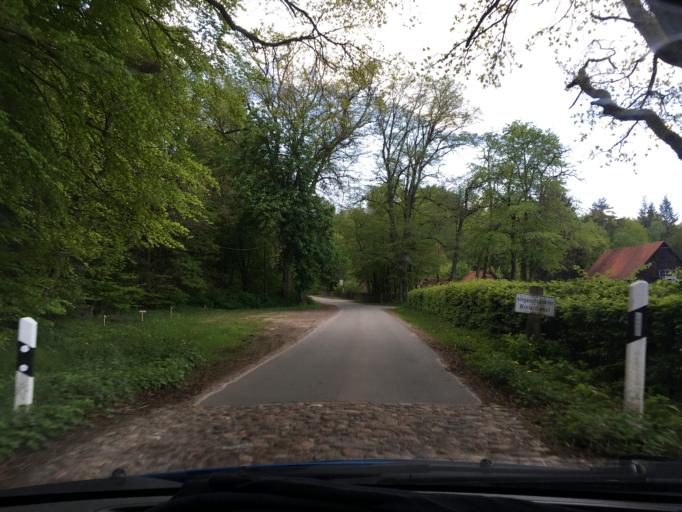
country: DE
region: Lower Saxony
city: Nahrendorf
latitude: 53.1419
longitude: 10.8069
